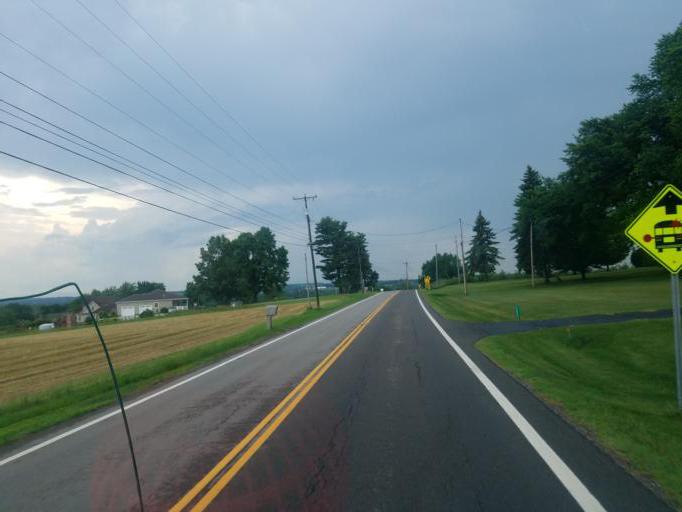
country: US
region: Ohio
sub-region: Wayne County
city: Doylestown
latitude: 40.9664
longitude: -81.7377
